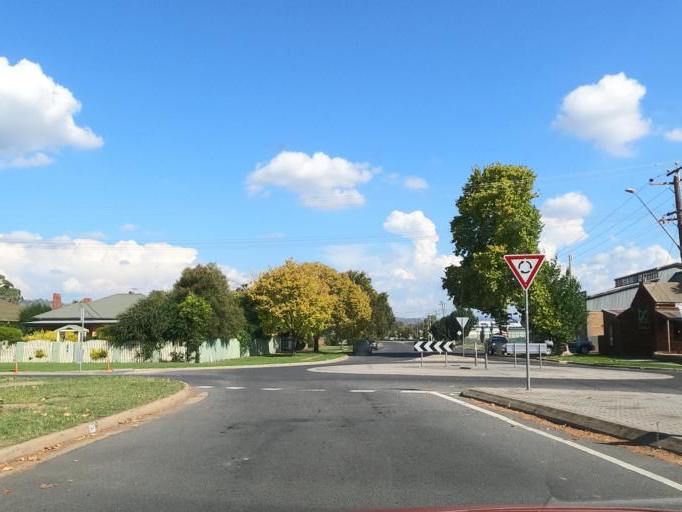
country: AU
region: New South Wales
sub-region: Albury Municipality
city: South Albury
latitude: -36.0864
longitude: 146.9121
